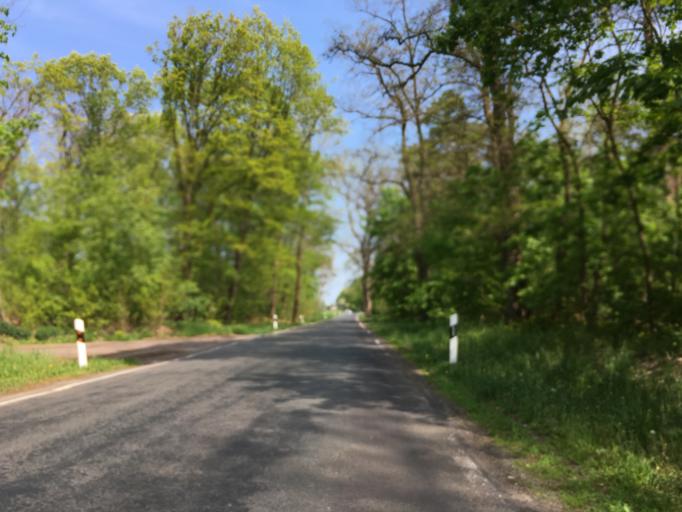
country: DE
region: Brandenburg
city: Werneuchen
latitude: 52.6689
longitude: 13.7332
